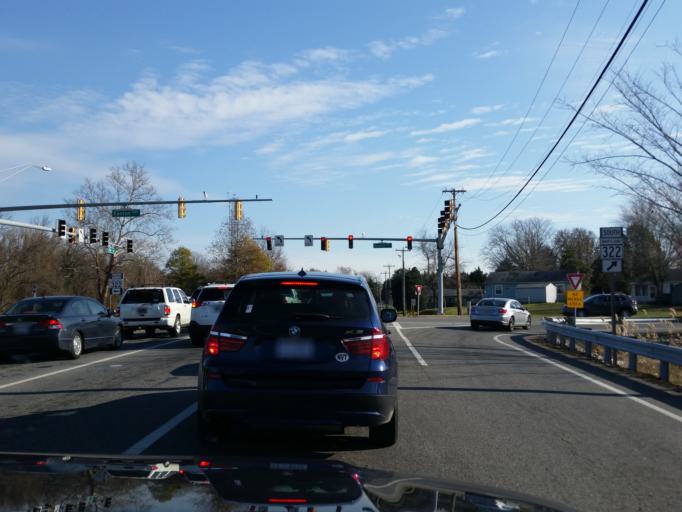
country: US
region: Maryland
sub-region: Talbot County
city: Easton
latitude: 38.7779
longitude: -76.0860
